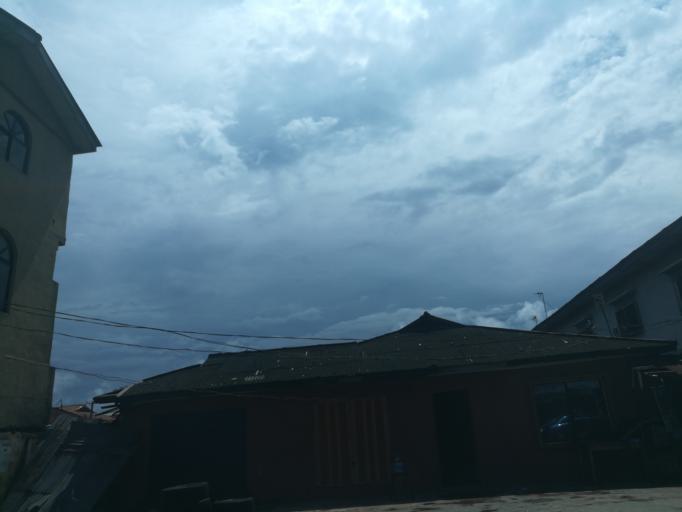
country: NG
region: Lagos
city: Agege
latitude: 6.6196
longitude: 3.3307
